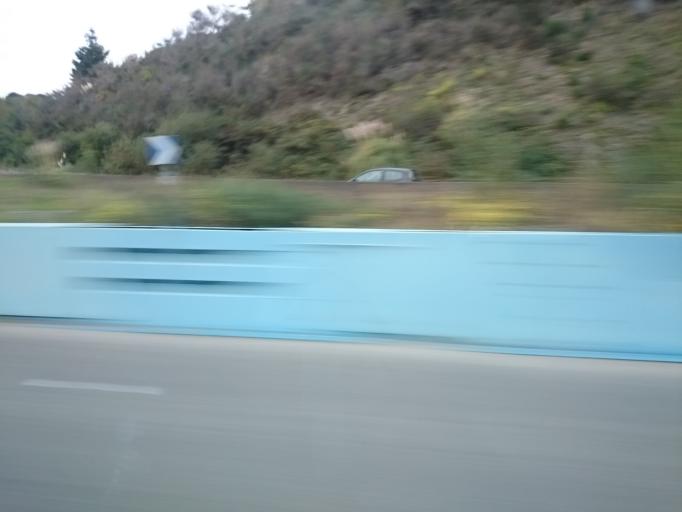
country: FR
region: Brittany
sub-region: Departement du Morbihan
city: Lorient
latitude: 47.7716
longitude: -3.3769
